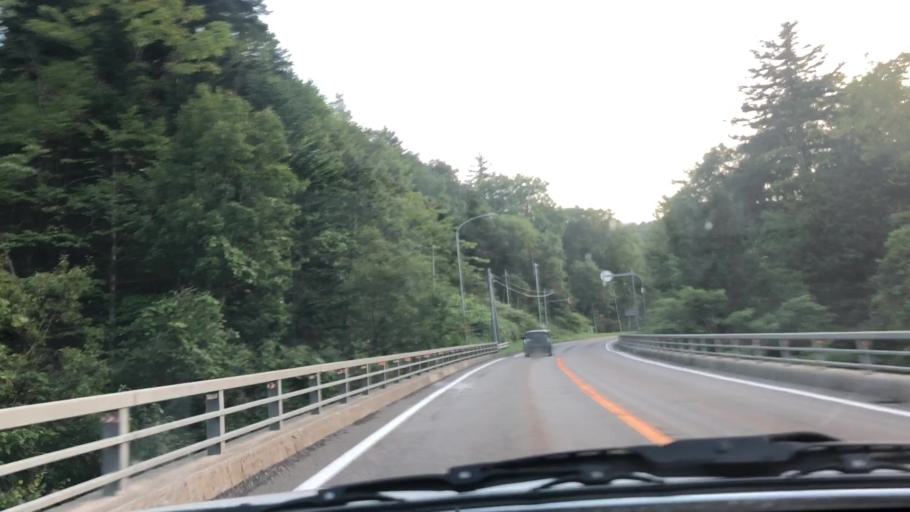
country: JP
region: Hokkaido
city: Shimo-furano
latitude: 42.8785
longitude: 142.2285
